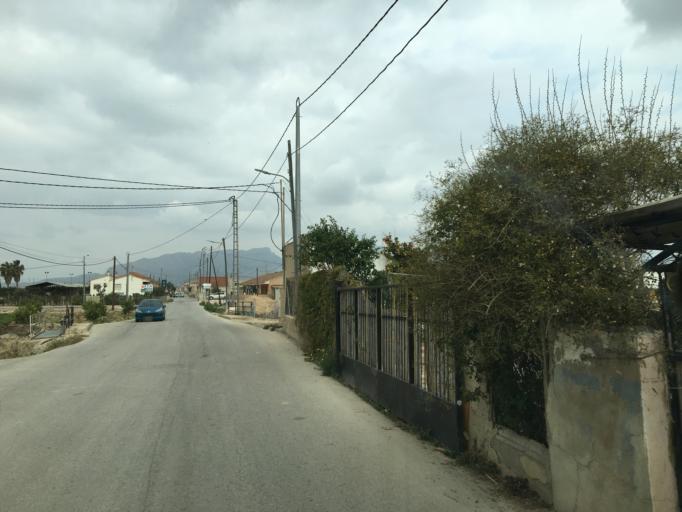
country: ES
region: Murcia
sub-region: Murcia
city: Beniel
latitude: 38.0316
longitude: -0.9825
